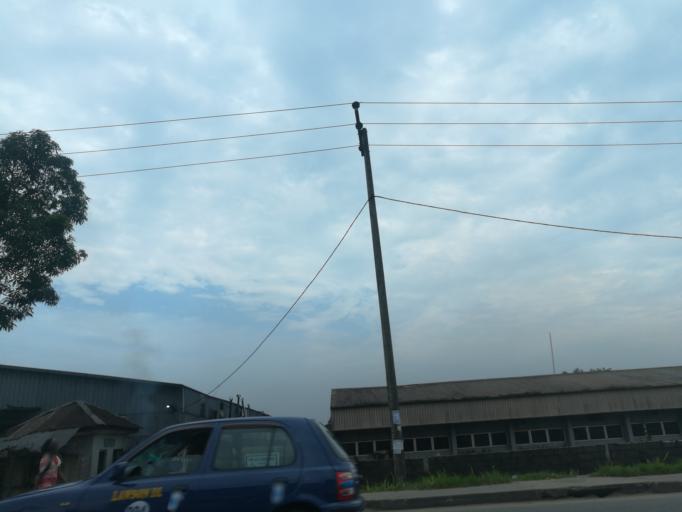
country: NG
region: Rivers
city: Port Harcourt
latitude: 4.8465
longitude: 6.9810
